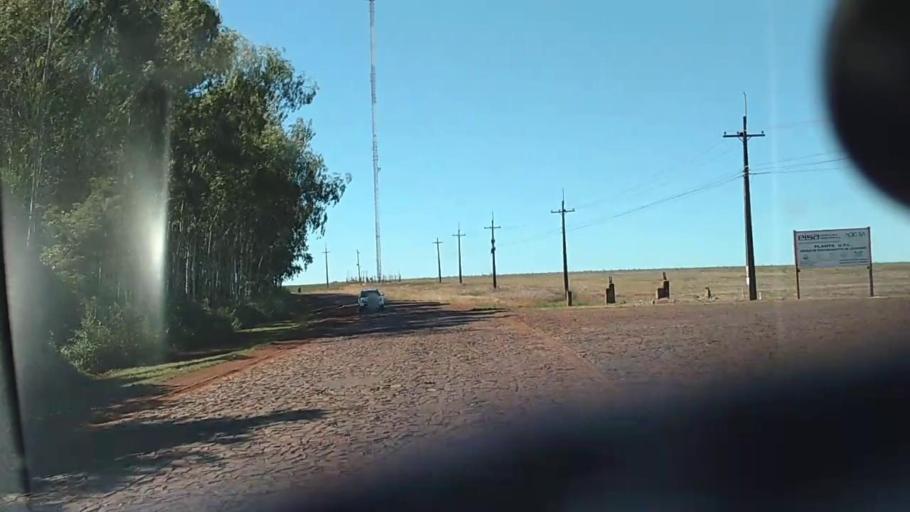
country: PY
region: Alto Parana
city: Naranjal
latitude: -25.9769
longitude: -55.1616
